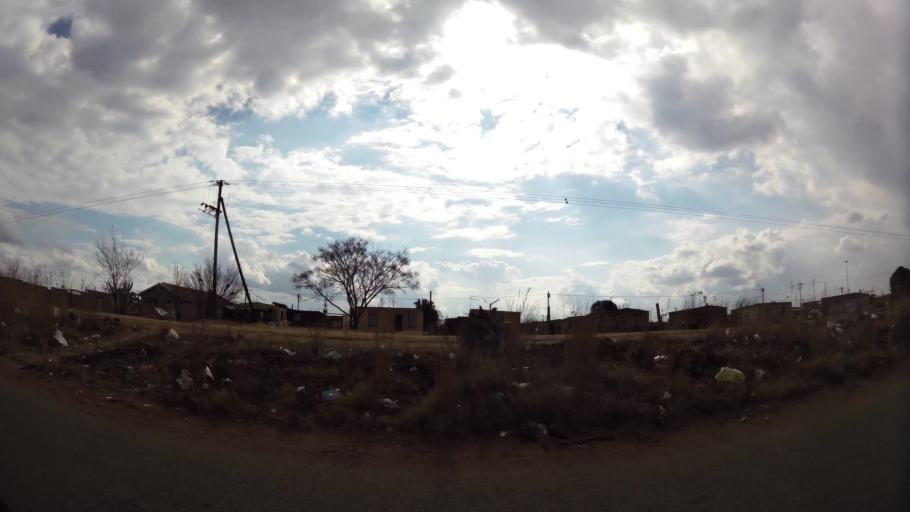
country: ZA
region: Gauteng
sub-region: Sedibeng District Municipality
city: Vanderbijlpark
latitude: -26.6804
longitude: 27.7882
